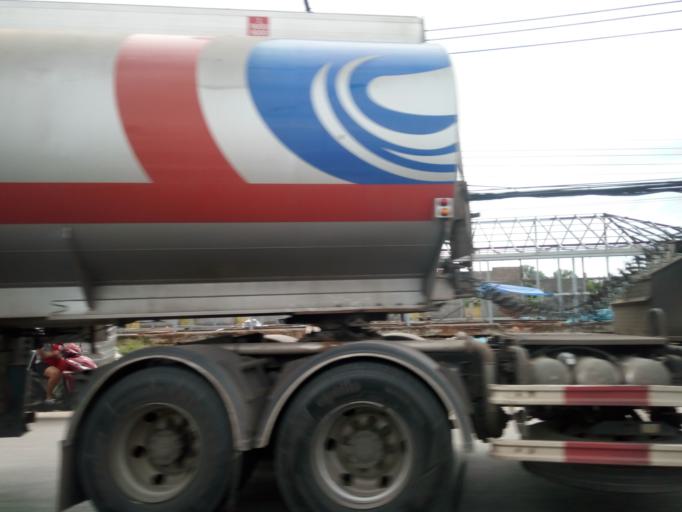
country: TH
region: Phuket
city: Thalang
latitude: 8.0958
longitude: 98.3059
